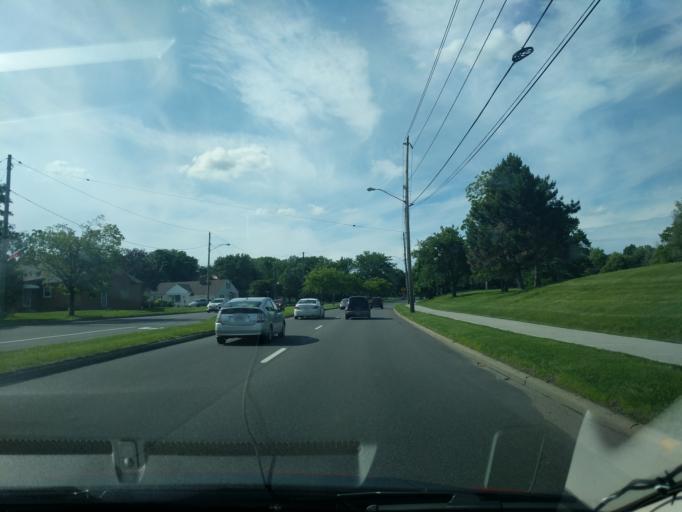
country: US
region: Ohio
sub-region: Cuyahoga County
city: Warrensville Heights
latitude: 41.4470
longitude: -81.5322
